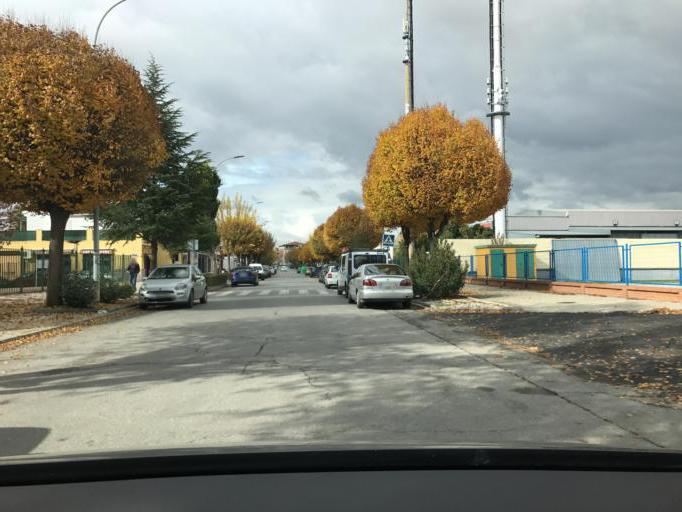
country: ES
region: Andalusia
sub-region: Provincia de Granada
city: Albolote
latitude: 37.2292
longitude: -3.6480
